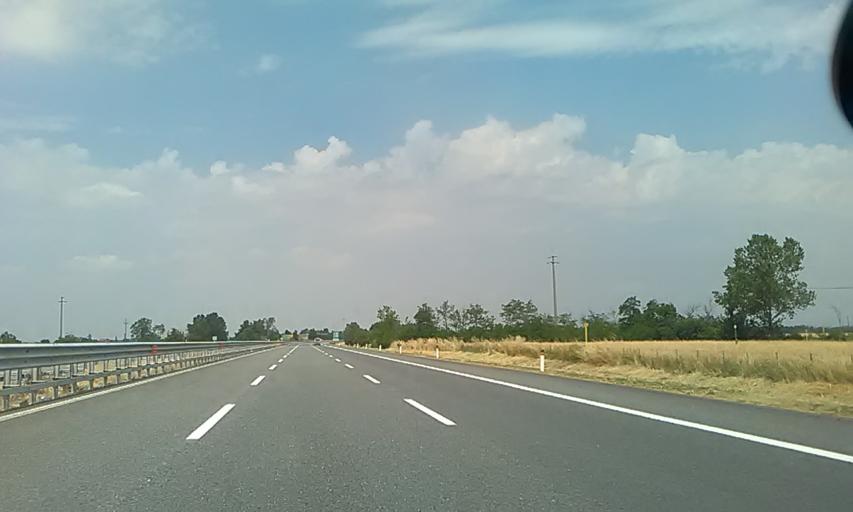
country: IT
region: Piedmont
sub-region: Provincia di Alessandria
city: Castelspina
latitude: 44.8094
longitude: 8.5991
